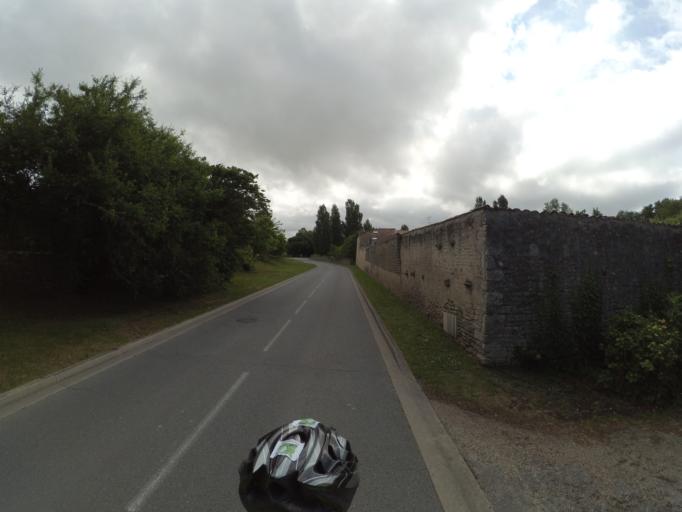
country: FR
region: Poitou-Charentes
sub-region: Departement de la Charente-Maritime
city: Chatelaillon-Plage
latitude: 46.0578
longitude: -1.0811
